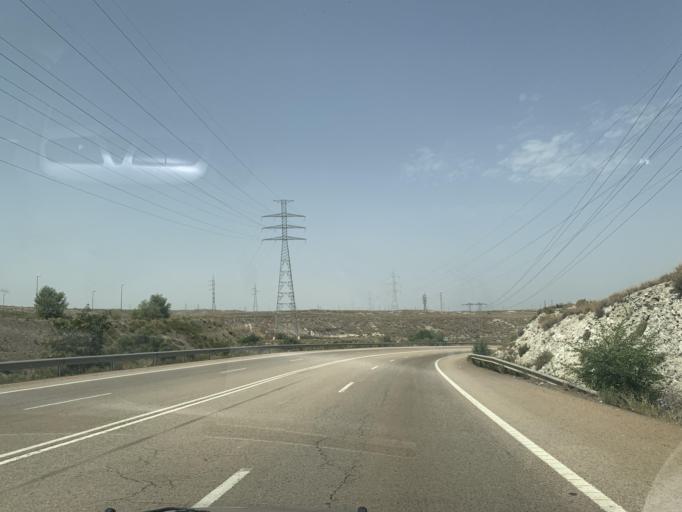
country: ES
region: Aragon
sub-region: Provincia de Zaragoza
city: Zaragoza
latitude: 41.5927
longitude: -0.8342
